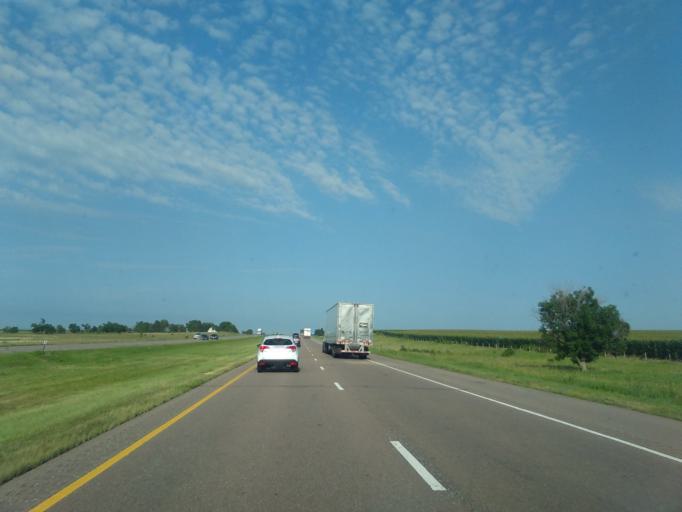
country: US
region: Nebraska
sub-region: York County
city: York
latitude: 40.8212
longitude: -97.6731
